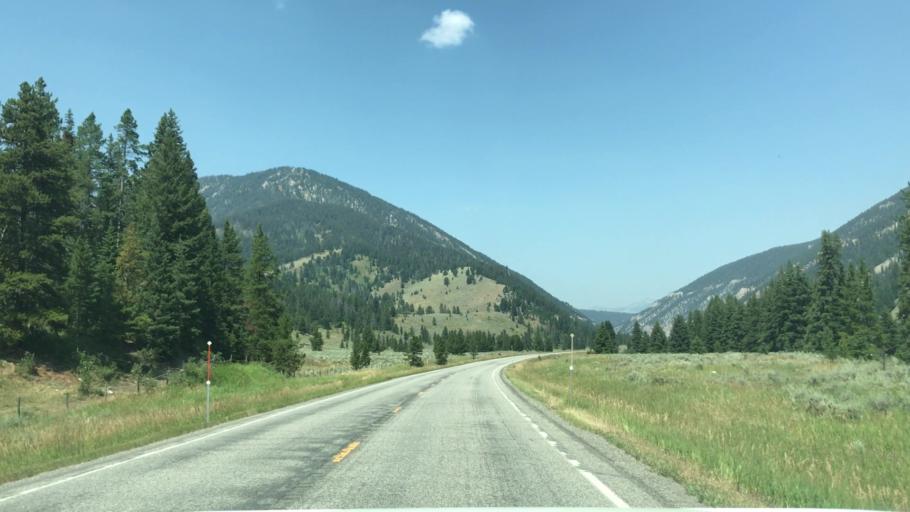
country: US
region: Montana
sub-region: Gallatin County
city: Big Sky
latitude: 45.1031
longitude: -111.2203
